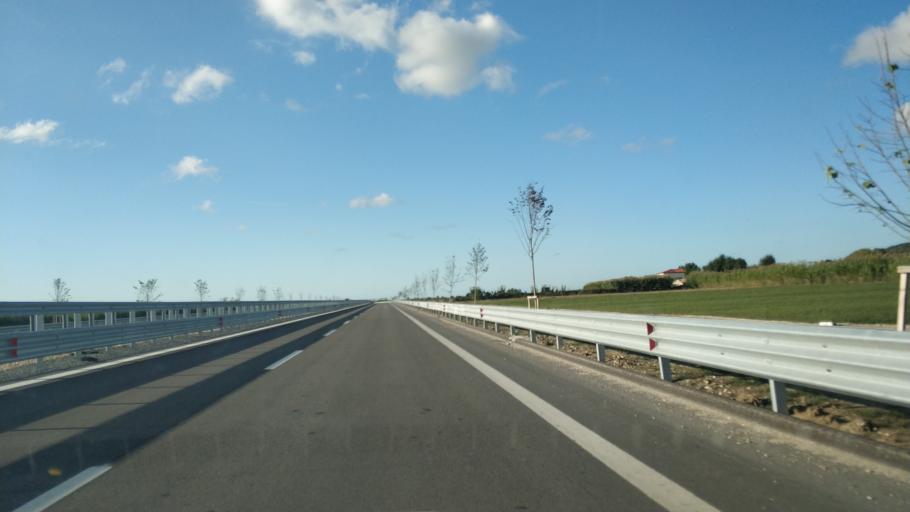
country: AL
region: Fier
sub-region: Rrethi i Fierit
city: Levan
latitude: 40.6975
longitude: 19.4644
